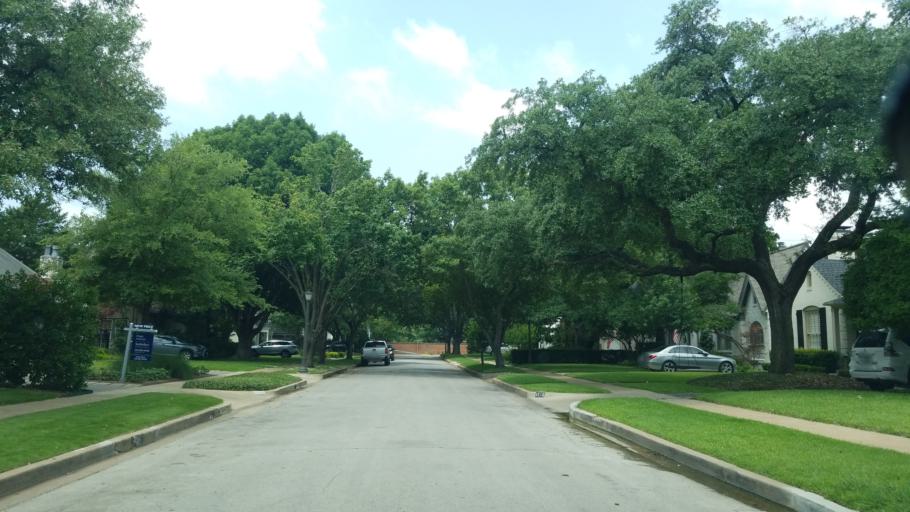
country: US
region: Texas
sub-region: Dallas County
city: University Park
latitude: 32.8357
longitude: -96.8136
